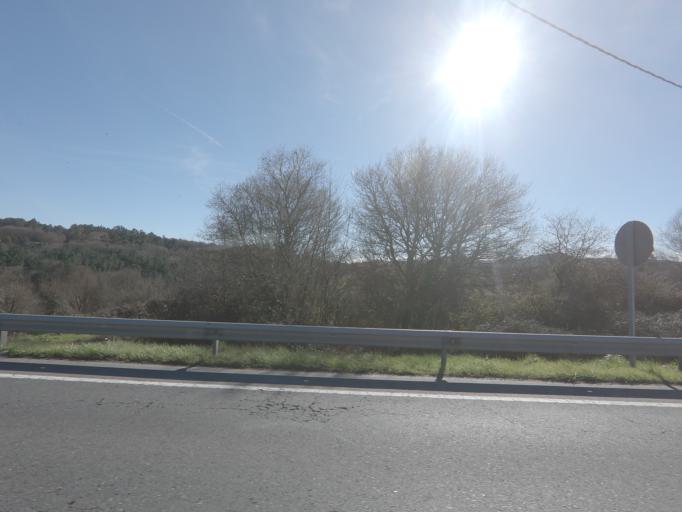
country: ES
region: Galicia
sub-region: Provincia de Pontevedra
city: Silleda
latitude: 42.6869
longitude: -8.2054
